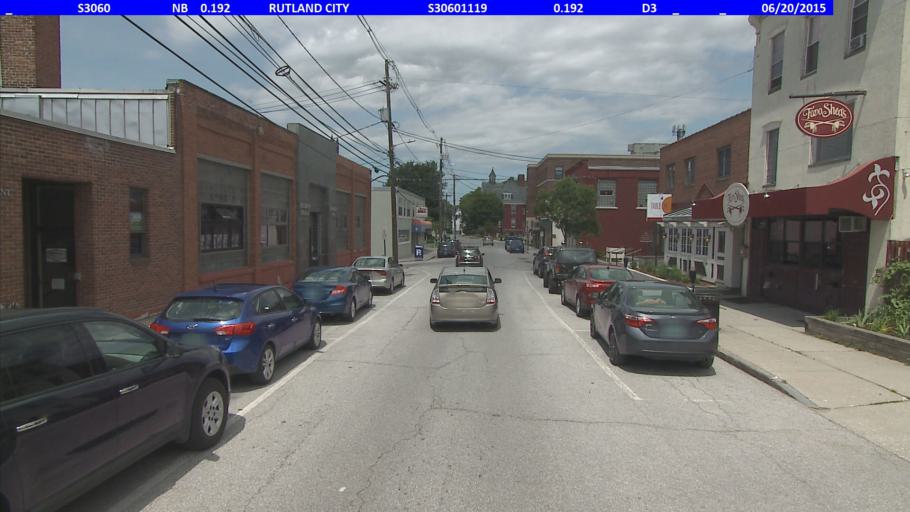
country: US
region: Vermont
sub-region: Rutland County
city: Rutland
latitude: 43.6070
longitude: -72.9776
